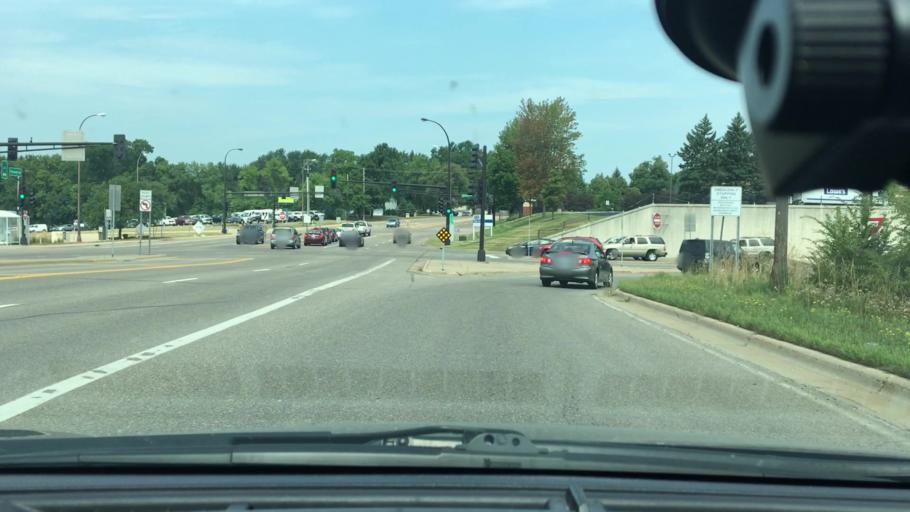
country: US
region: Minnesota
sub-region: Hennepin County
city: Minnetonka Mills
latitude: 44.9717
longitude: -93.4453
